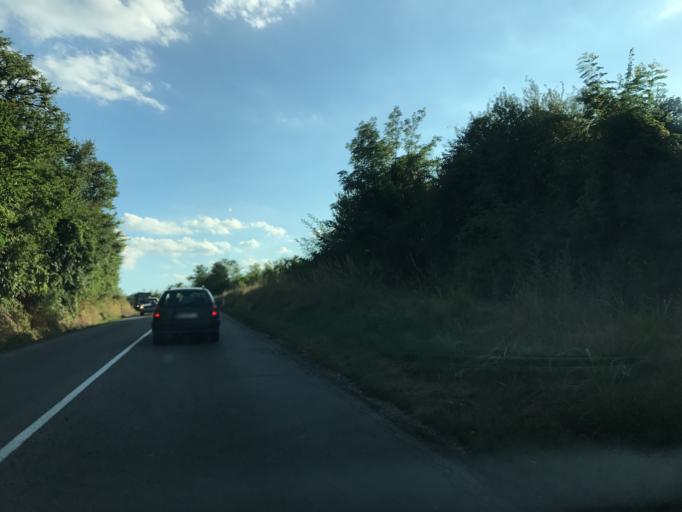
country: RS
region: Central Serbia
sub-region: Belgrade
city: Grocka
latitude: 44.7031
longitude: 20.6623
